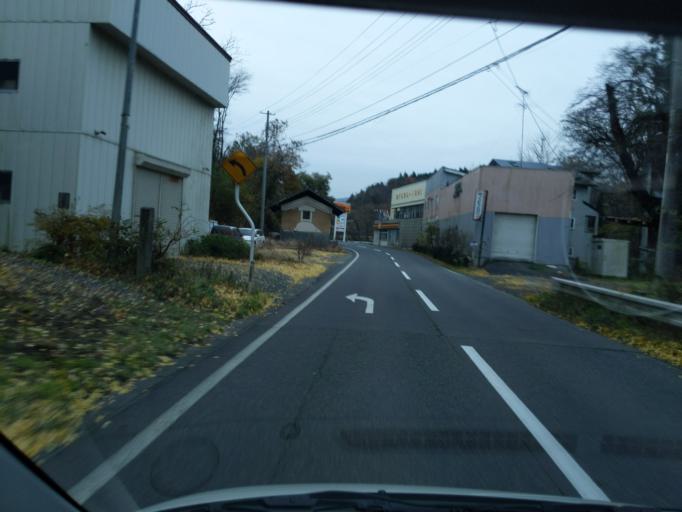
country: JP
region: Iwate
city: Kitakami
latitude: 39.2278
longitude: 141.2526
